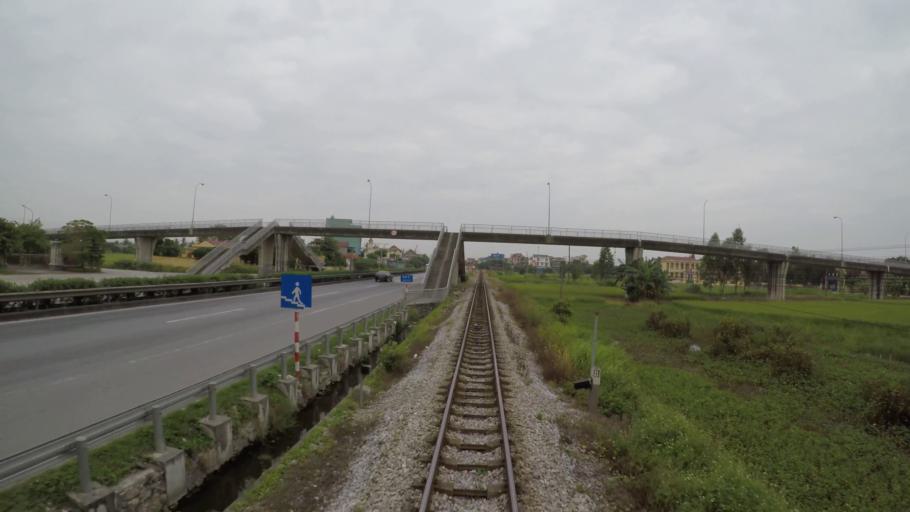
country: VN
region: Hai Duong
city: Phu Thai
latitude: 20.9558
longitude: 106.5274
